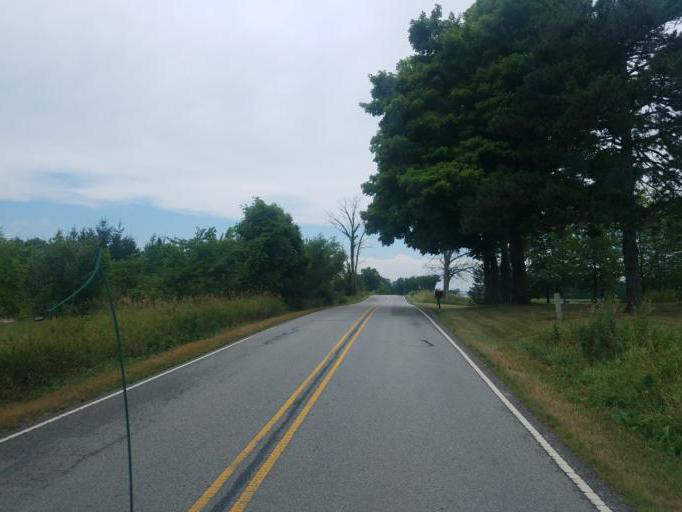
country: US
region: Indiana
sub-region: DeKalb County
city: Butler
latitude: 41.3866
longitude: -84.8331
